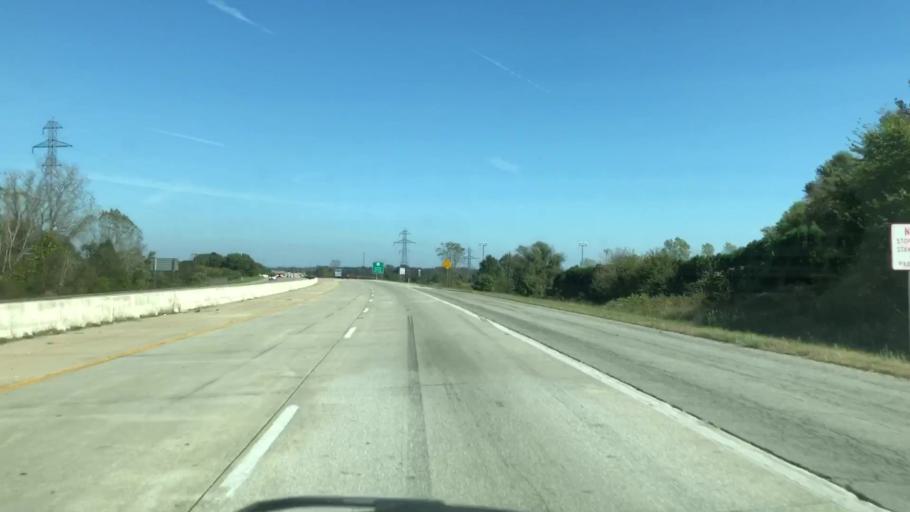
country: US
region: Indiana
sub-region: Elkhart County
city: Elkhart
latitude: 41.6399
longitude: -85.9683
